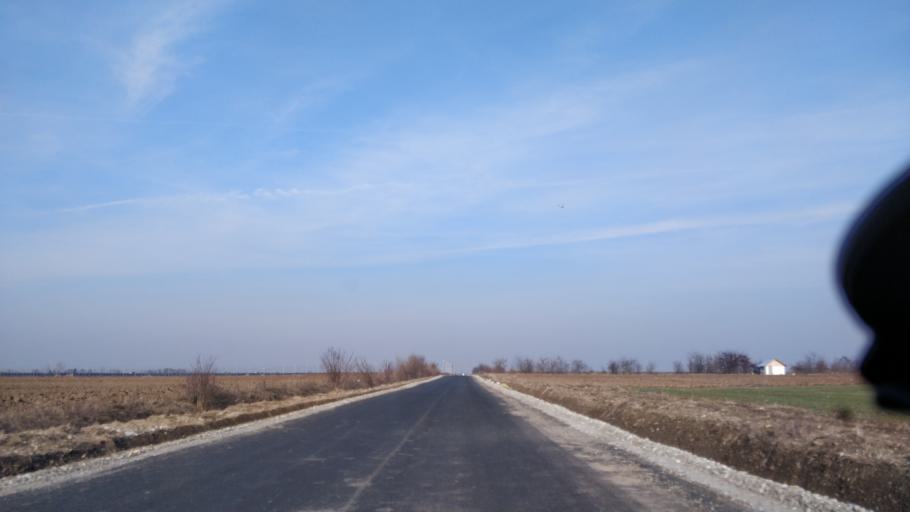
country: RO
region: Dambovita
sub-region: Comuna Brezoaiele
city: Brezoaia
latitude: 44.5334
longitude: 25.7937
